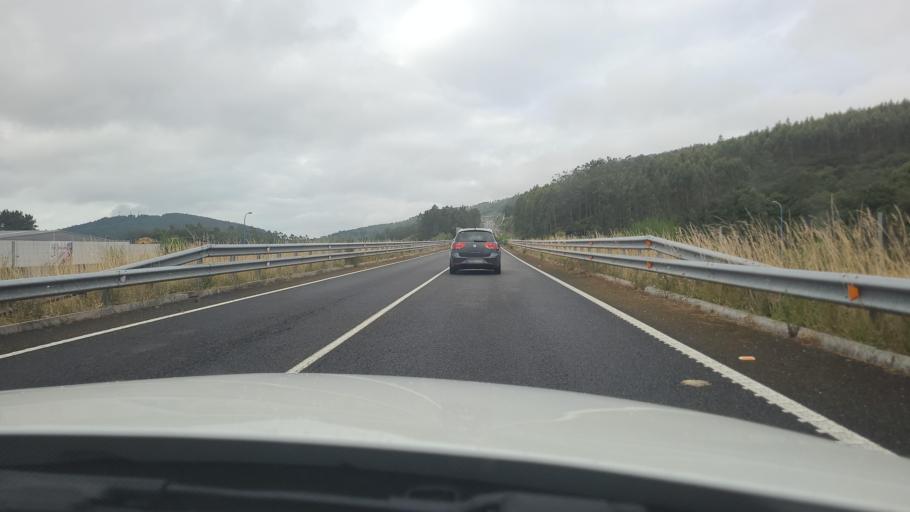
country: ES
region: Galicia
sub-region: Provincia da Coruna
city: Cee
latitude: 42.9760
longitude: -9.1923
